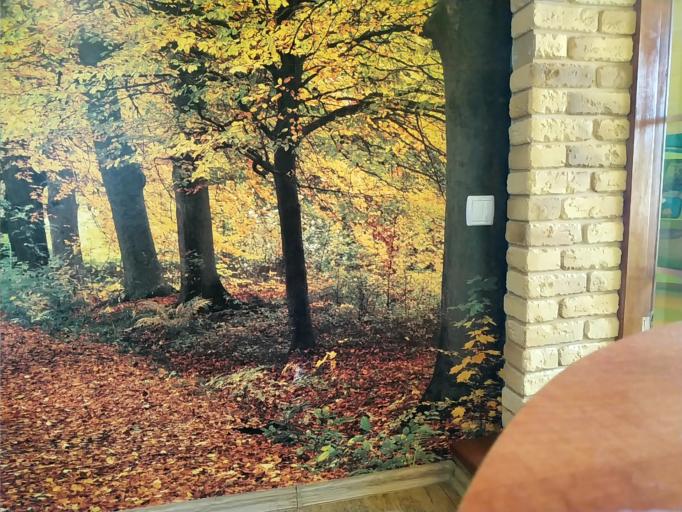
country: RU
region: Arkhangelskaya
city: Onega
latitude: 63.6699
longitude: 38.0966
